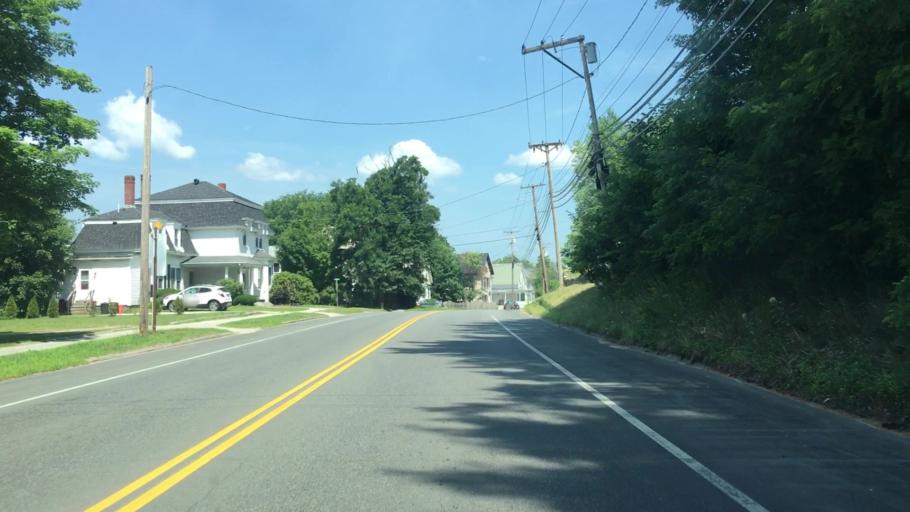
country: US
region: New Hampshire
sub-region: Sullivan County
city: Newport
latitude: 43.3685
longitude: -72.1766
